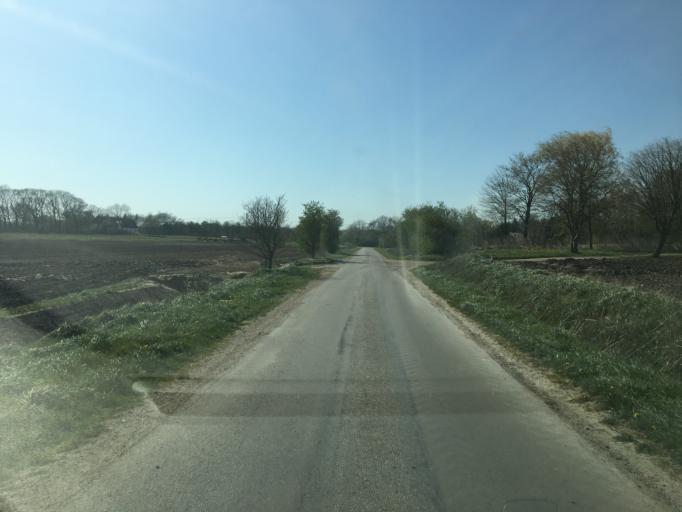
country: DK
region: South Denmark
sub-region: Aabenraa Kommune
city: Rodekro
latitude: 55.0967
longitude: 9.2424
